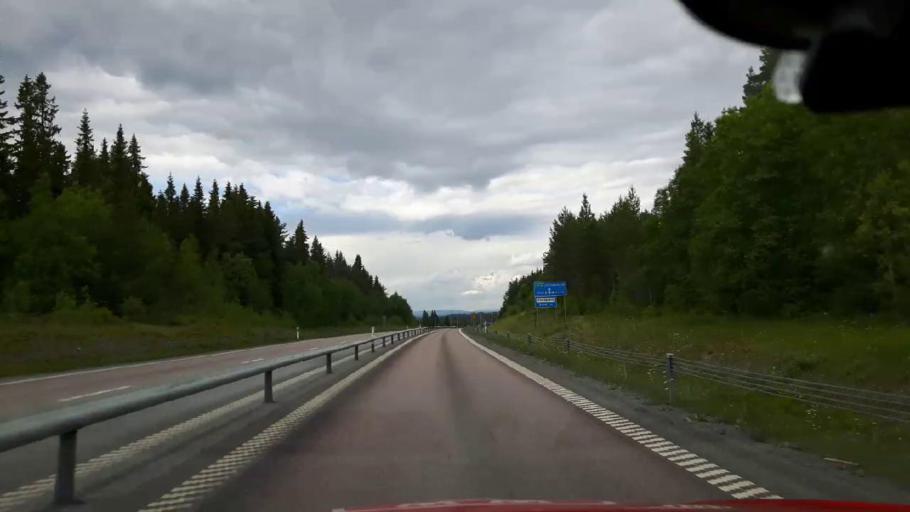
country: SE
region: Jaemtland
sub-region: Krokoms Kommun
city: Krokom
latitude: 63.2638
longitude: 14.5442
